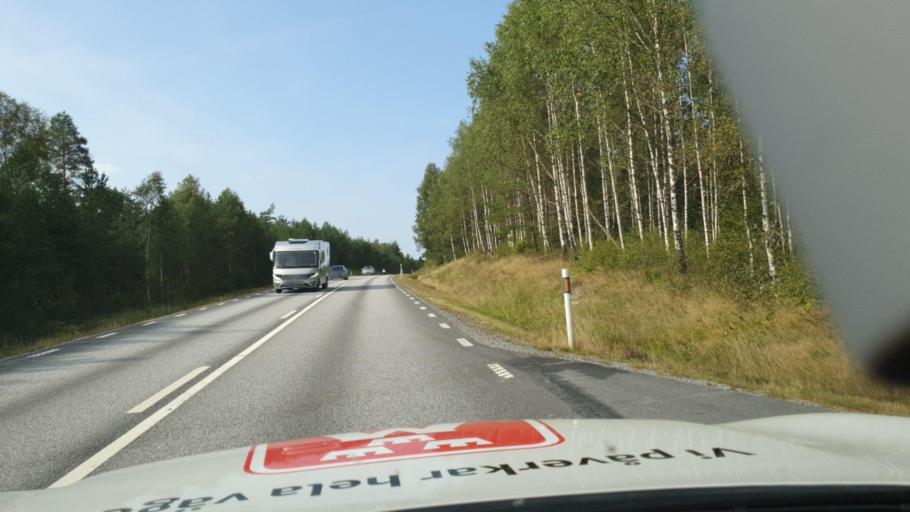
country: SE
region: Vaestra Goetaland
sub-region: Dals-Ed Kommun
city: Ed
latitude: 58.8474
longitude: 11.6786
